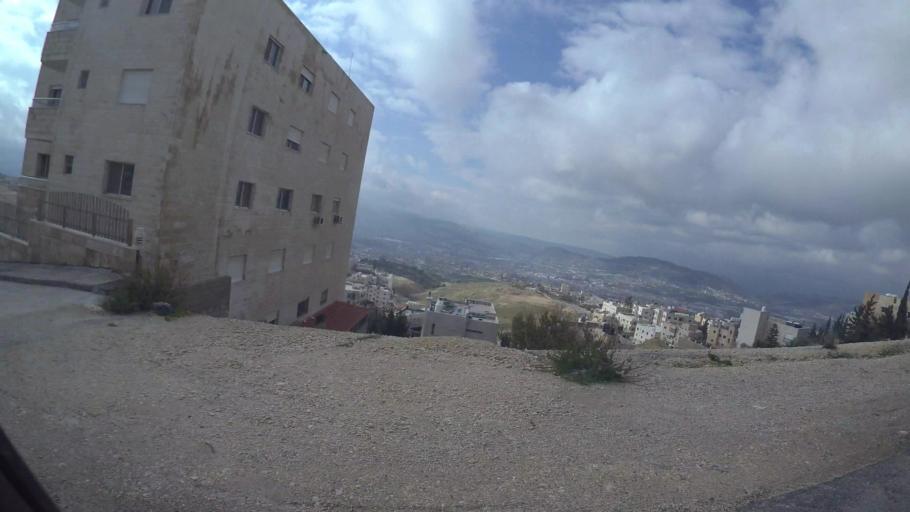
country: JO
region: Amman
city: Al Jubayhah
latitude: 32.0604
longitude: 35.8682
